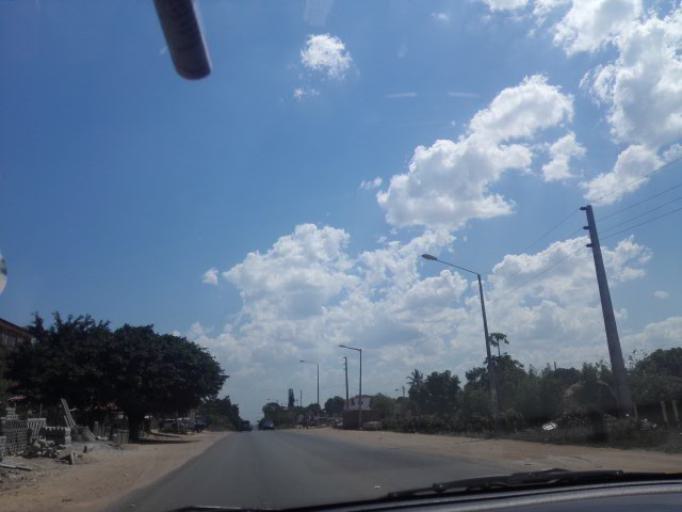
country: MZ
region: Maputo
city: Matola
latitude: -25.9592
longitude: 32.4509
